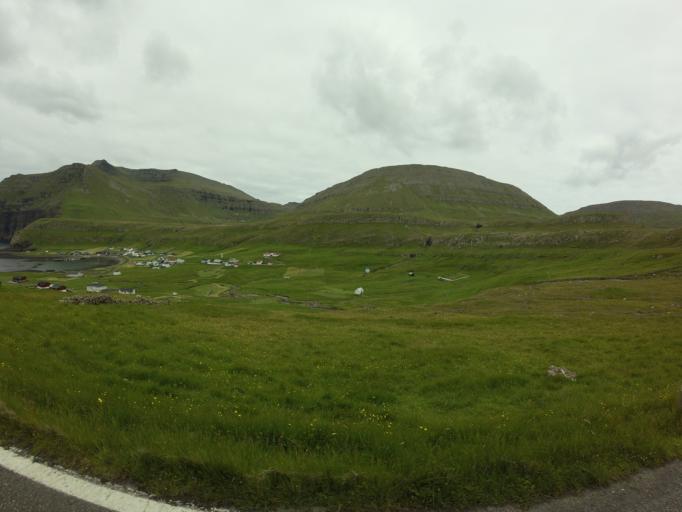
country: FO
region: Suduroy
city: Tvoroyri
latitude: 61.5181
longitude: -6.8774
